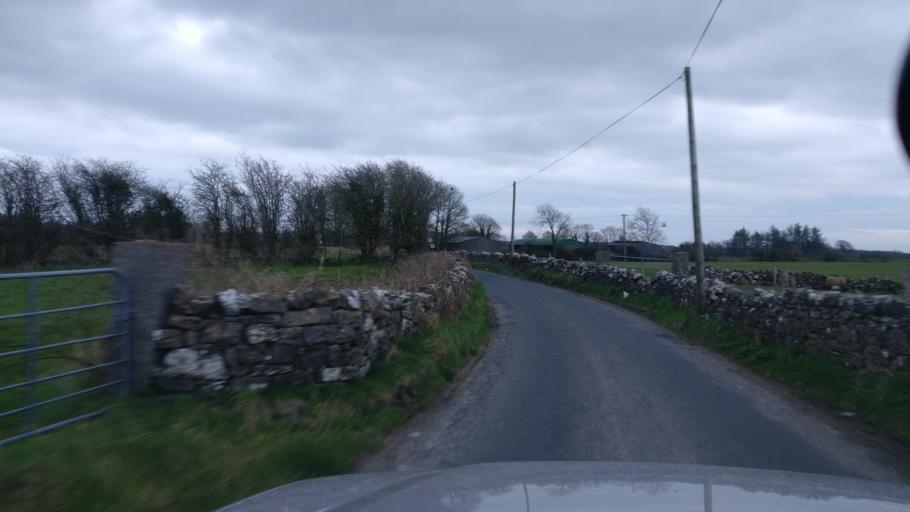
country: IE
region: Connaught
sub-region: County Galway
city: Loughrea
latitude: 53.2577
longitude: -8.4454
